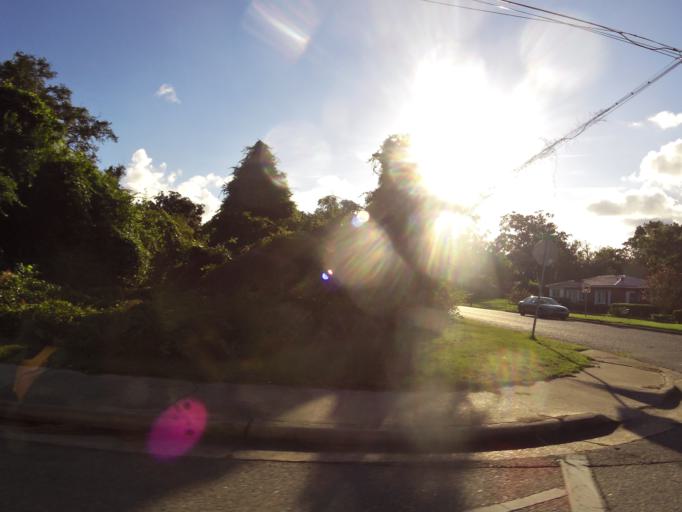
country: US
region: Georgia
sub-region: Glynn County
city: Brunswick
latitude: 31.1616
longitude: -81.4920
